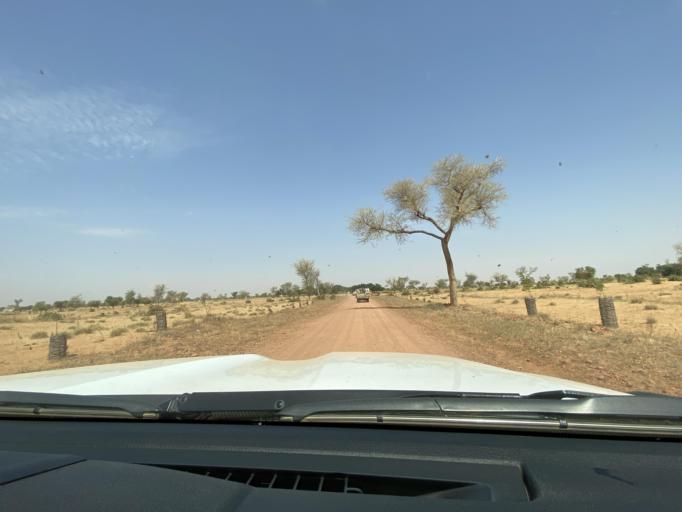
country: NE
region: Dosso
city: Birnin Gaoure
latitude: 13.2396
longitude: 2.8670
